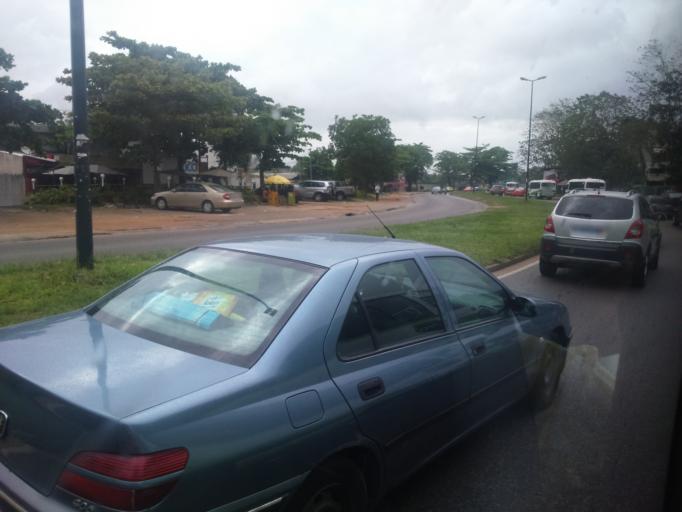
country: CI
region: Lagunes
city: Abobo
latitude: 5.3672
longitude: -3.9982
